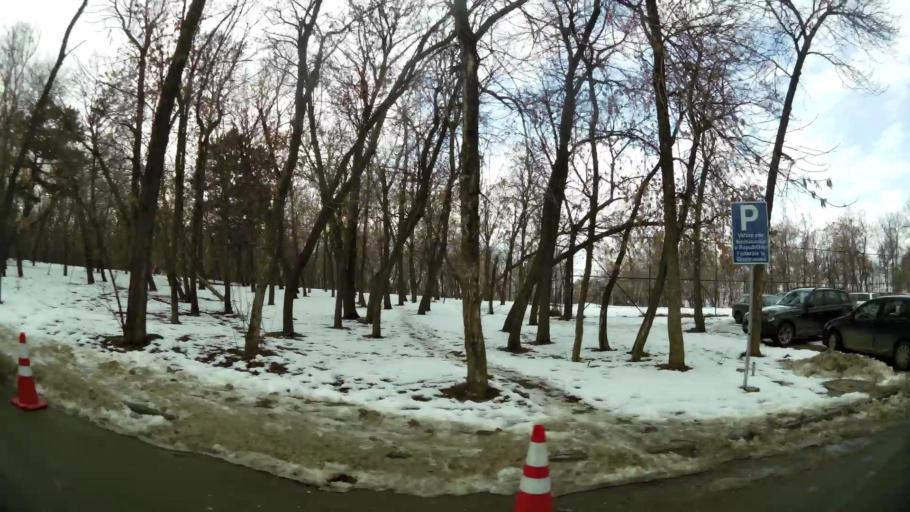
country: XK
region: Pristina
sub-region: Komuna e Prishtines
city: Pristina
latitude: 42.6690
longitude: 21.1529
